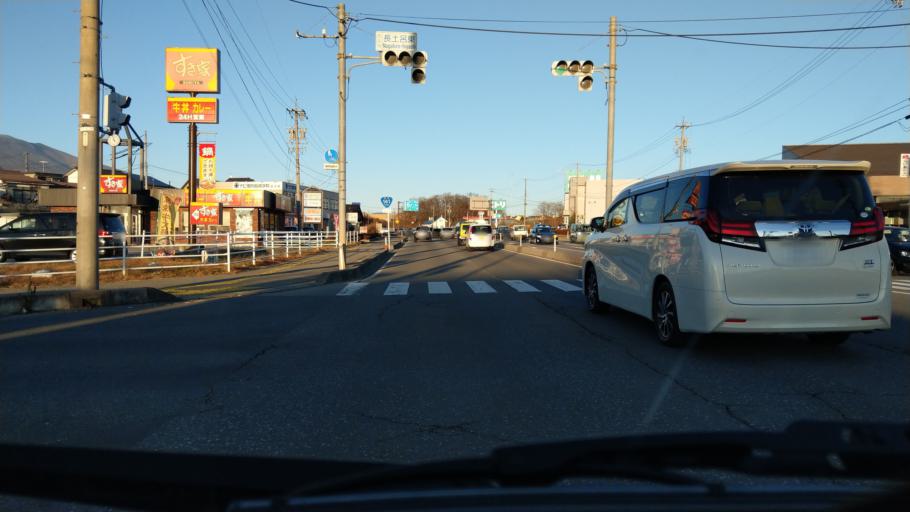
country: JP
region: Nagano
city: Komoro
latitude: 36.2805
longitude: 138.4699
